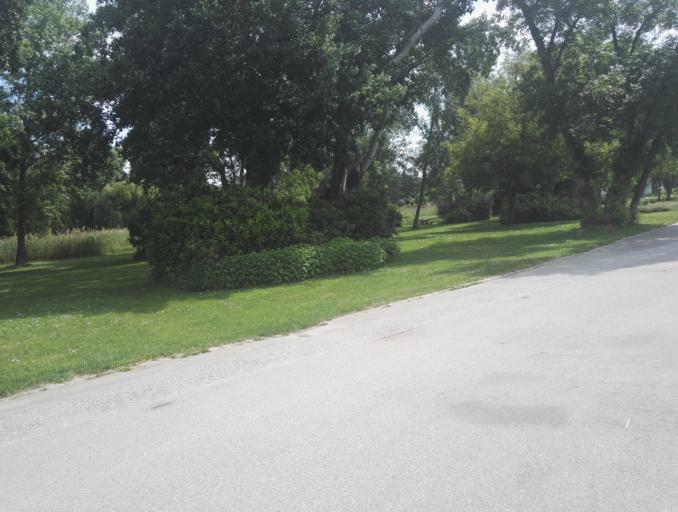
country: AT
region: Vienna
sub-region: Wien Stadt
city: Vienna
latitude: 48.2395
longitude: 16.4131
